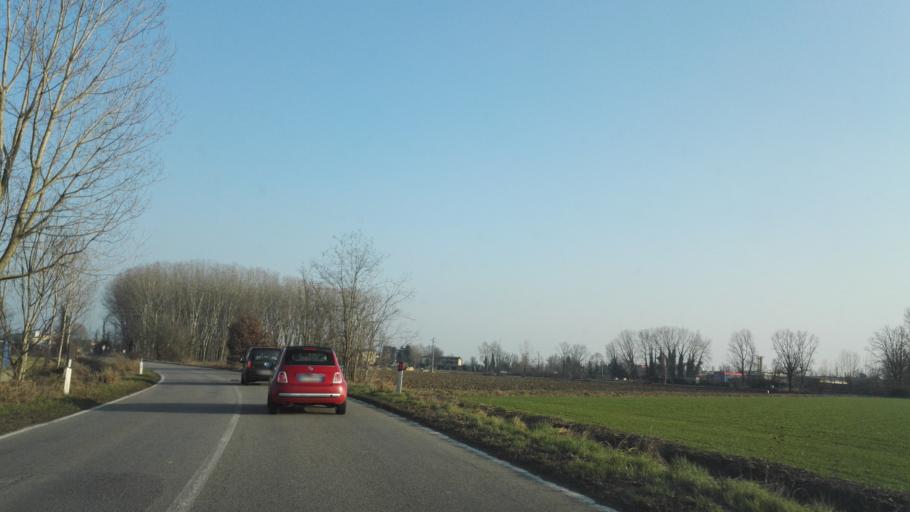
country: IT
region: Lombardy
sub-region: Citta metropolitana di Milano
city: Tribiano
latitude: 45.4208
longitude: 9.3805
